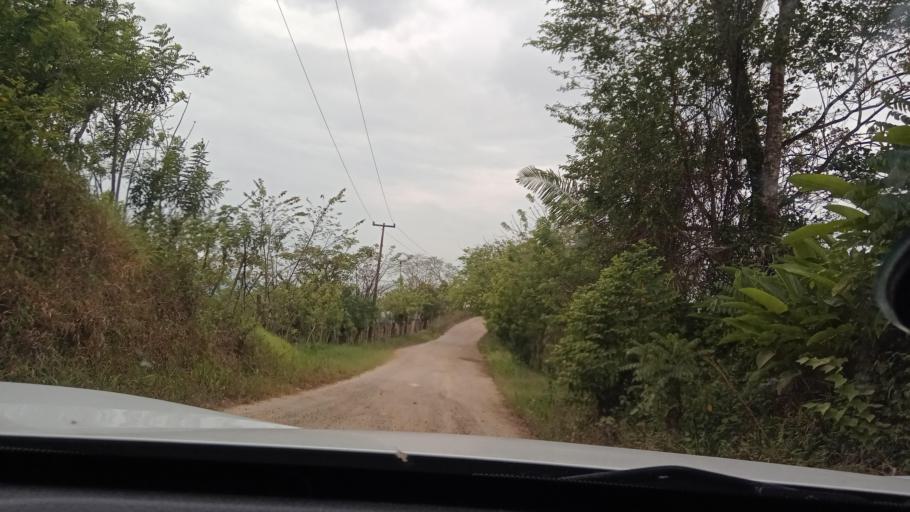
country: MX
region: Tabasco
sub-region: Huimanguillo
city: Francisco Rueda
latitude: 17.5800
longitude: -94.0646
